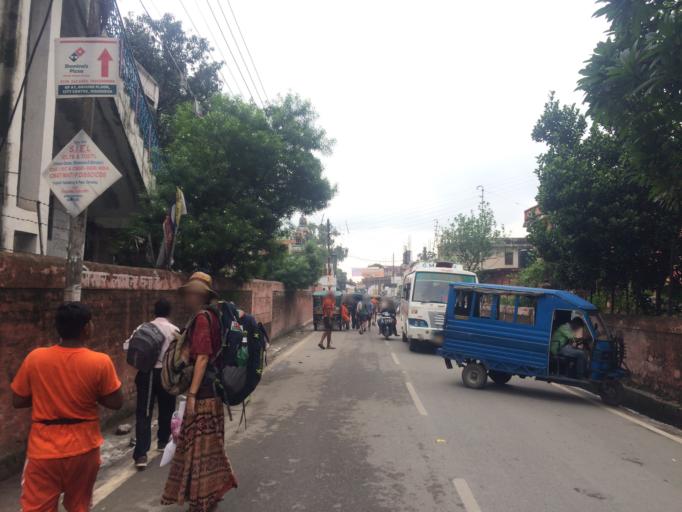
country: IN
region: Uttarakhand
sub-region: Dehradun
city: Rishikesh
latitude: 30.1174
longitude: 78.3044
